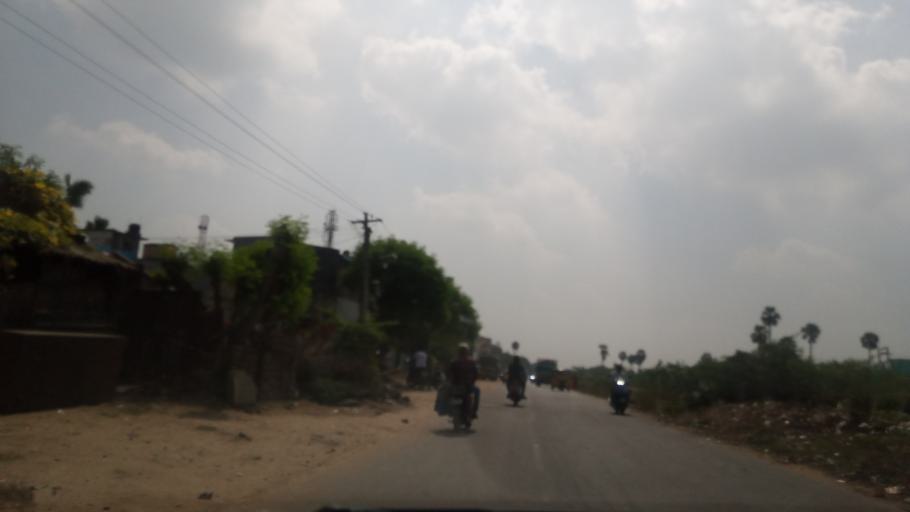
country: IN
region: Tamil Nadu
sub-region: Vellore
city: Arakkonam
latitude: 13.0732
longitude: 79.6715
